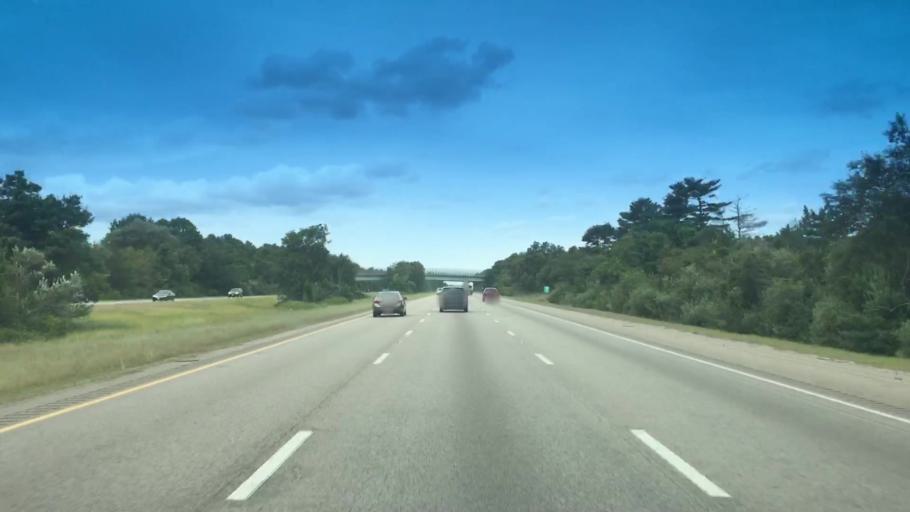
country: US
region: Massachusetts
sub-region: Bristol County
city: Norton Center
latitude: 41.9932
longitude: -71.1789
